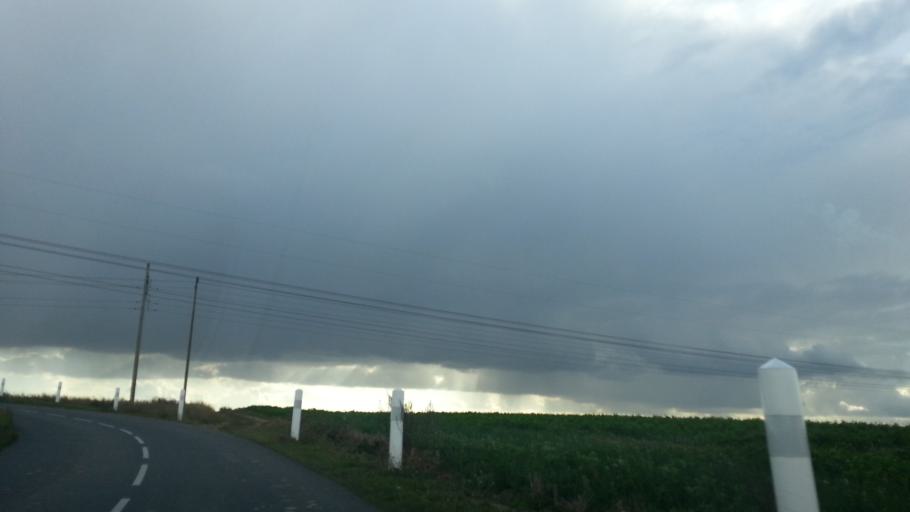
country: FR
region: Picardie
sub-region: Departement de l'Oise
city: Thiverny
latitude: 49.2488
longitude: 2.4032
